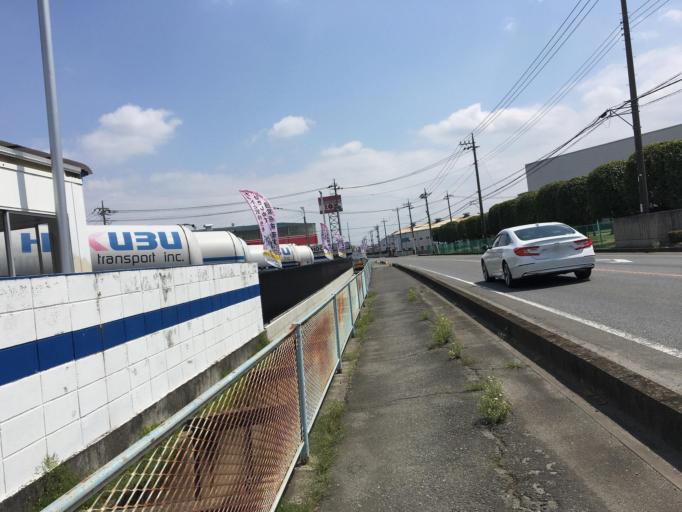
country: JP
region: Gunma
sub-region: Sawa-gun
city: Tamamura
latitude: 36.2926
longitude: 139.1433
